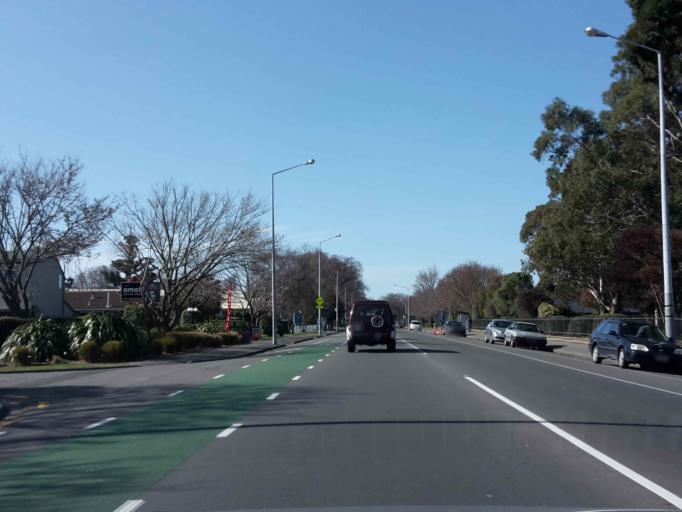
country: NZ
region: Canterbury
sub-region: Selwyn District
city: Prebbleton
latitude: -43.5345
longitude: 172.5629
